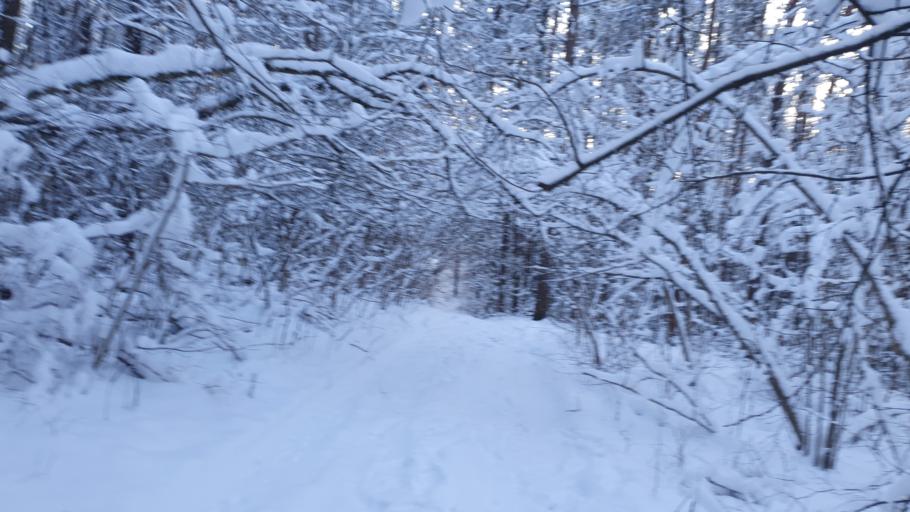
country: LT
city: Skaidiskes
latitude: 54.6433
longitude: 25.4170
